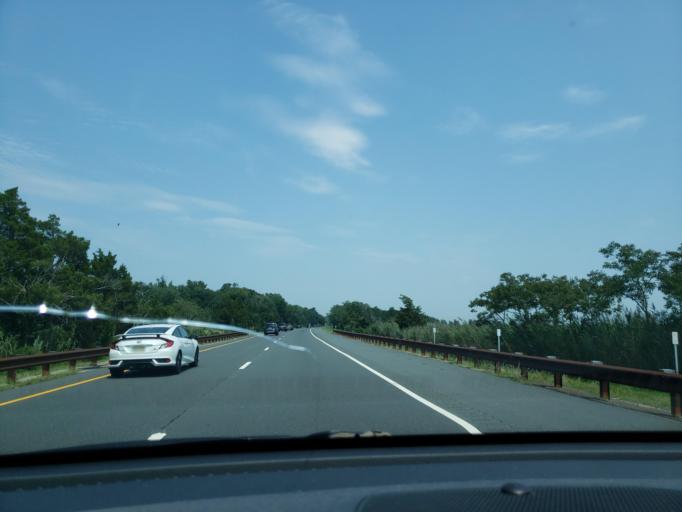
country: US
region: New Jersey
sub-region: Cape May County
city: Sea Isle City
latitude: 39.2088
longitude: -74.6946
